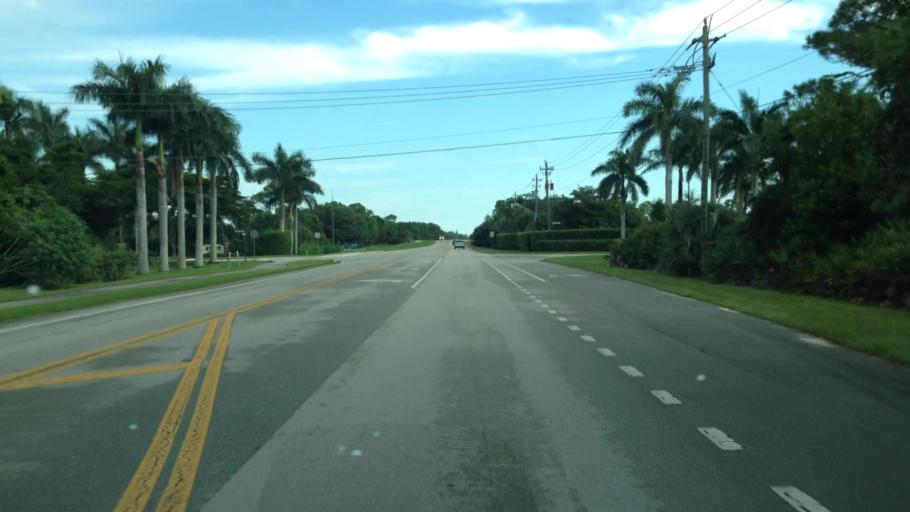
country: US
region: Florida
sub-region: Lee County
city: Bonita Springs
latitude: 26.3121
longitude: -81.8189
